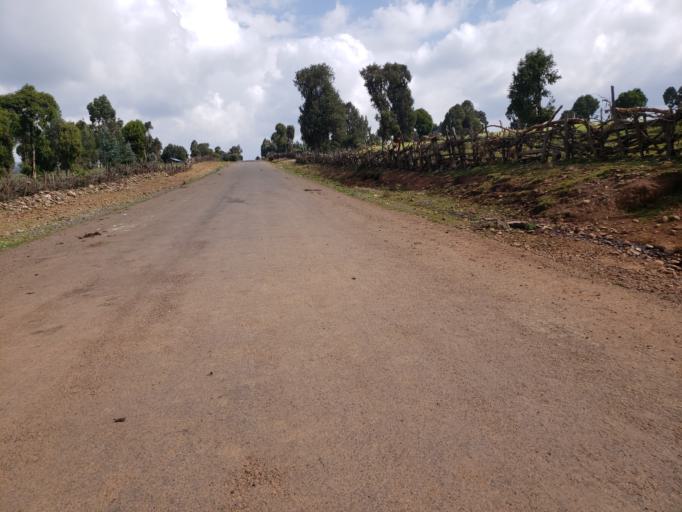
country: ET
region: Oromiya
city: Dodola
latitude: 6.8700
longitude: 39.3880
